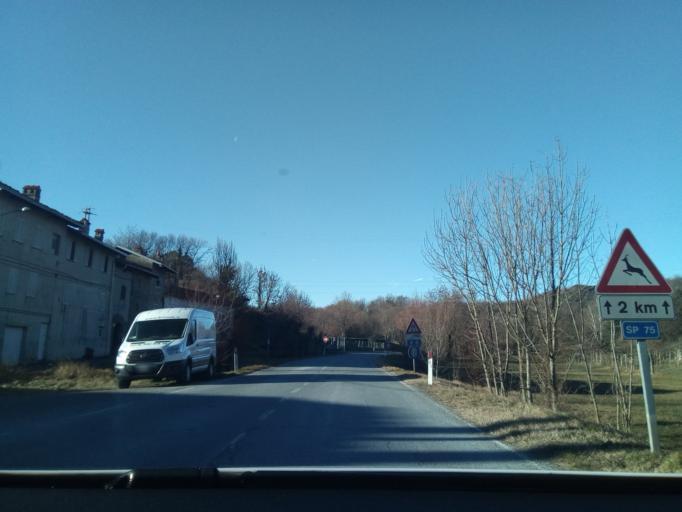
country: IT
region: Piedmont
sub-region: Provincia di Torino
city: Chiaverano
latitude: 45.4966
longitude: 7.8988
